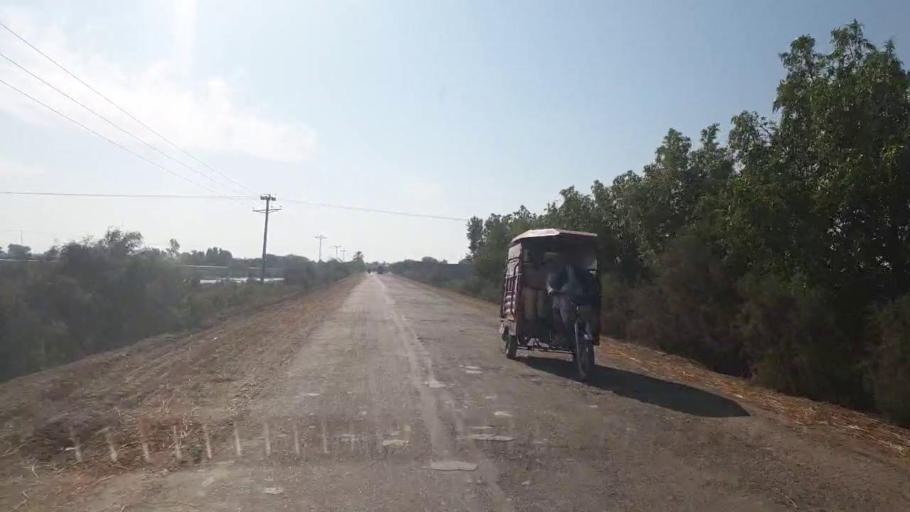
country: PK
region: Sindh
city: Talhar
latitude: 24.8992
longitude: 68.8248
